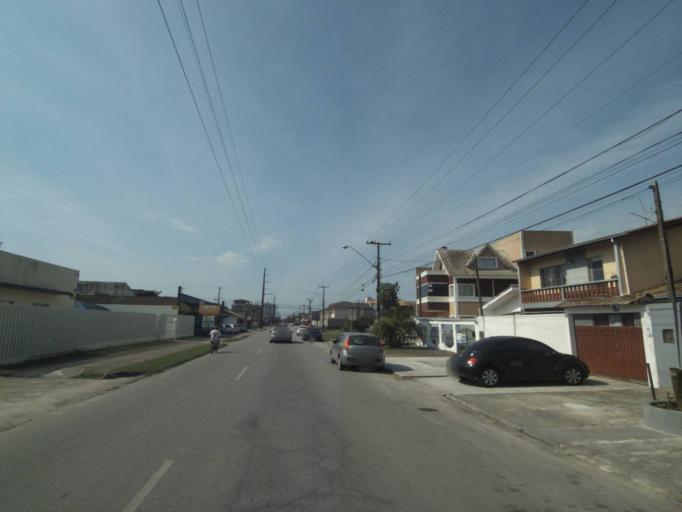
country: BR
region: Parana
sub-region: Paranagua
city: Paranagua
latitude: -25.5245
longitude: -48.5238
